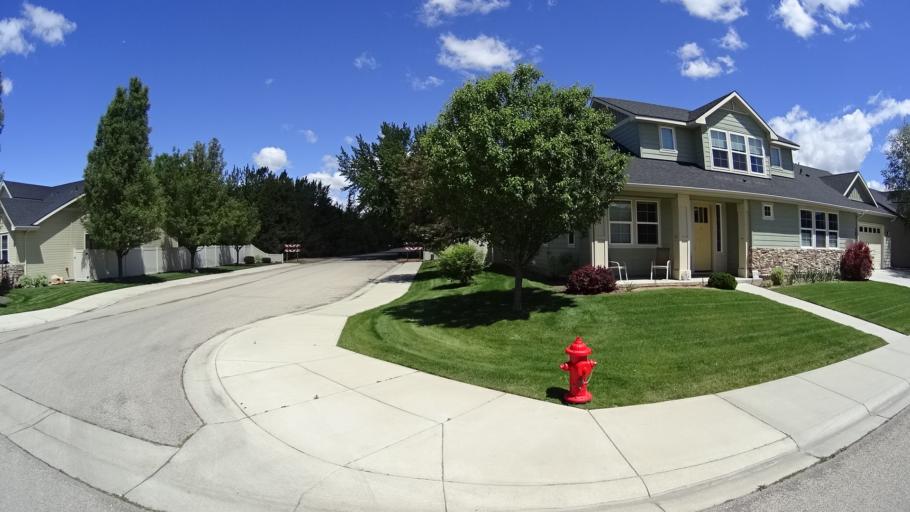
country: US
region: Idaho
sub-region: Ada County
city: Meridian
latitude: 43.6281
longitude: -116.3468
